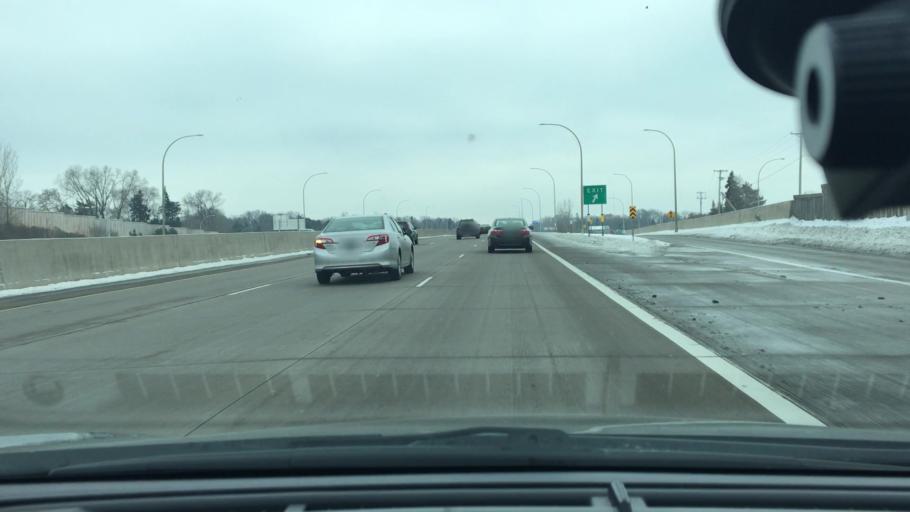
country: US
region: Minnesota
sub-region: Hennepin County
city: Golden Valley
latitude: 45.0026
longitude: -93.3495
